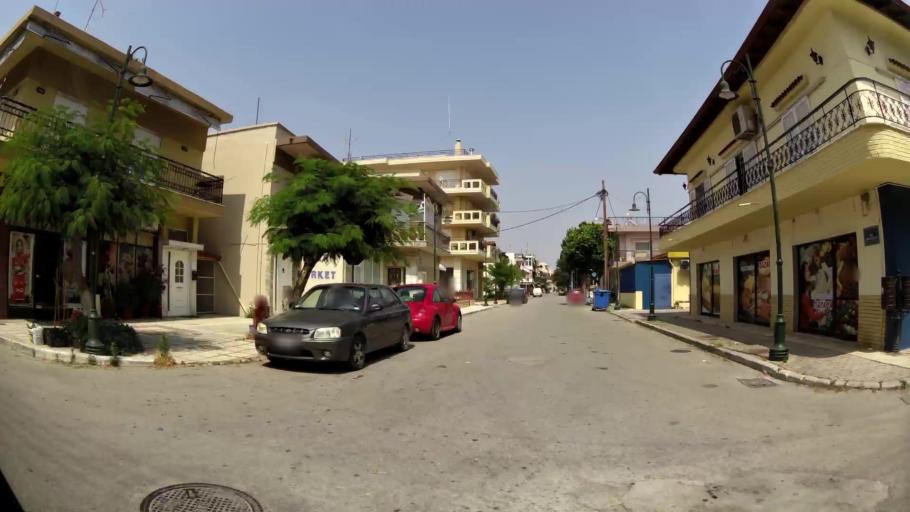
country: GR
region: Central Macedonia
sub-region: Nomos Thessalonikis
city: Nea Magnisia
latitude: 40.6882
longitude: 22.8420
